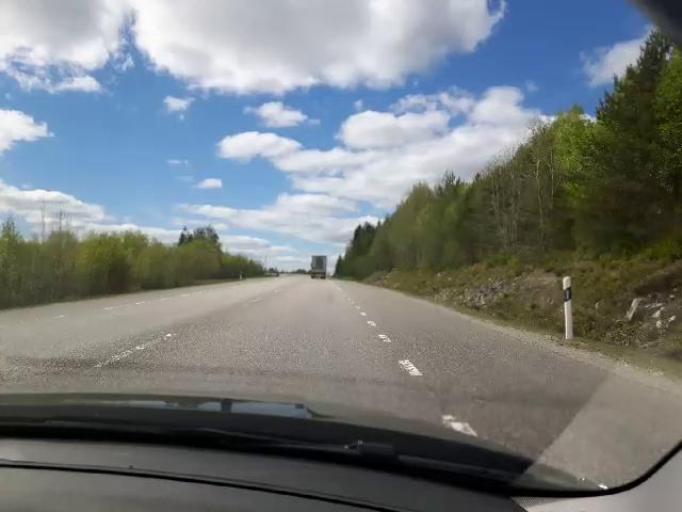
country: SE
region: Vaesternorrland
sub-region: Kramfors Kommun
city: Nordingra
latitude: 63.0046
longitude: 18.2500
